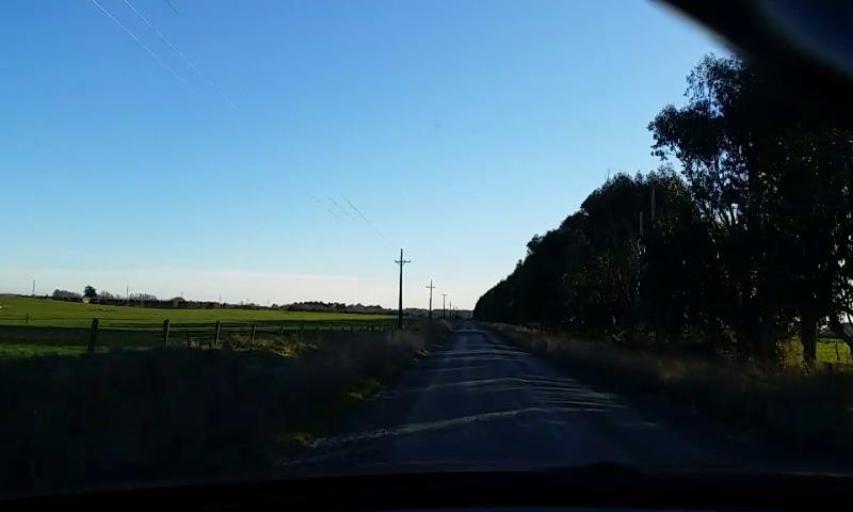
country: NZ
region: Southland
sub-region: Invercargill City
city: Invercargill
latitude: -46.2918
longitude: 168.4453
